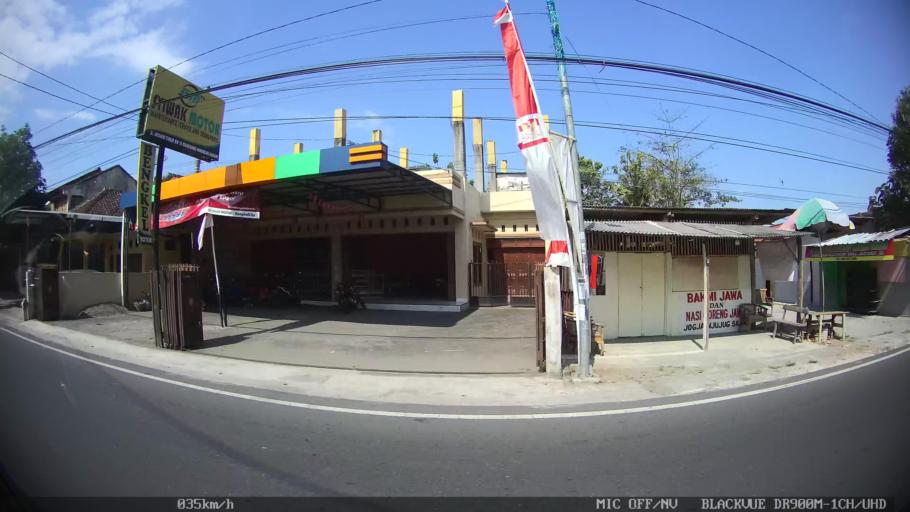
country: ID
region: Daerah Istimewa Yogyakarta
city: Sewon
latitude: -7.9119
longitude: 110.3827
